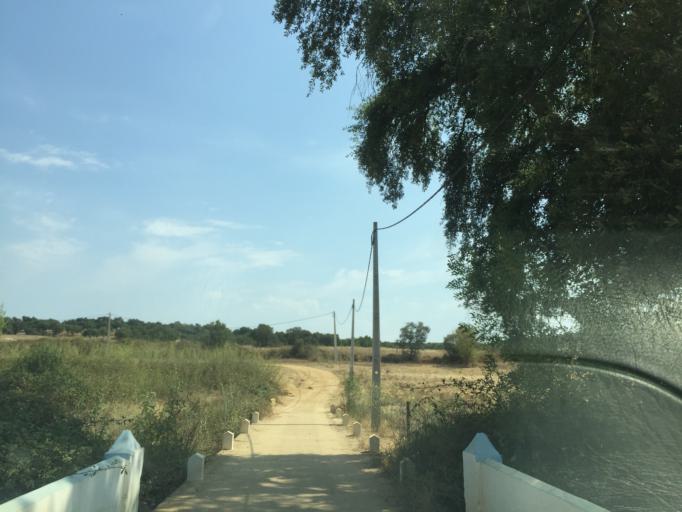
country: PT
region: Setubal
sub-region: Santiago do Cacem
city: Santiago do Cacem
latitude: 37.9721
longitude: -8.5032
